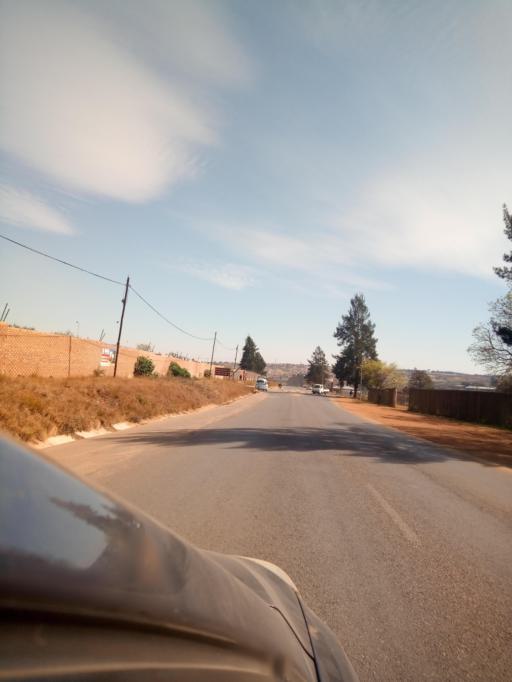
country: ZA
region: Mpumalanga
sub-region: Gert Sibande District Municipality
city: Piet Retief
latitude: -27.0162
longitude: 30.8043
